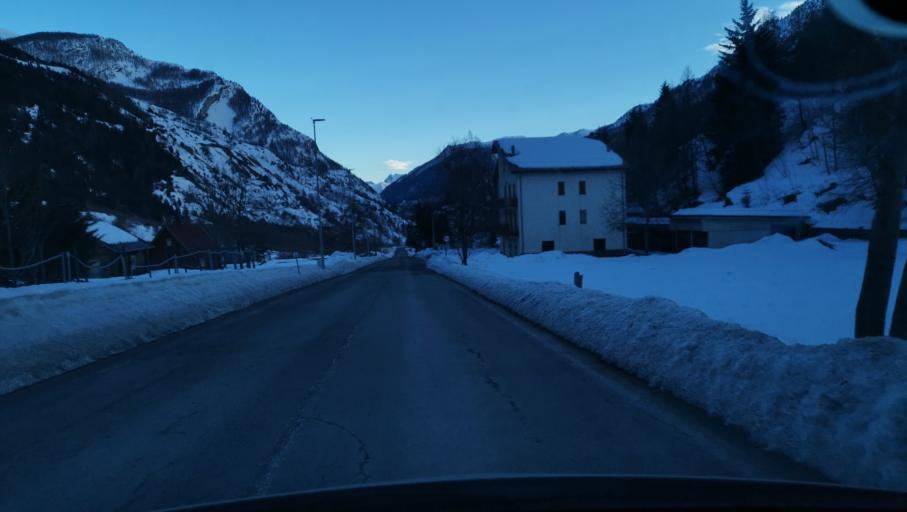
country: IT
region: Piedmont
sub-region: Provincia di Cuneo
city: Bersezio
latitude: 44.3714
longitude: 6.9788
